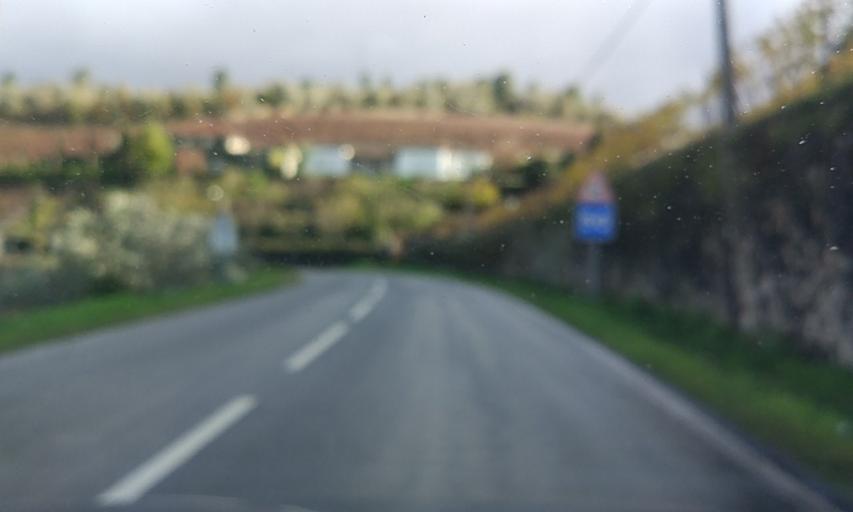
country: PT
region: Viseu
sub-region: Lamego
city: Lamego
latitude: 41.1288
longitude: -7.7935
